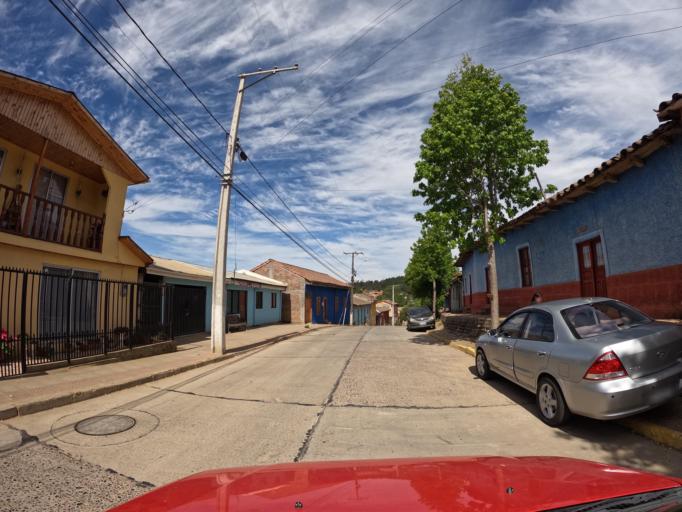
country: CL
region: Maule
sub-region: Provincia de Talca
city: Constitucion
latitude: -35.0961
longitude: -72.0181
